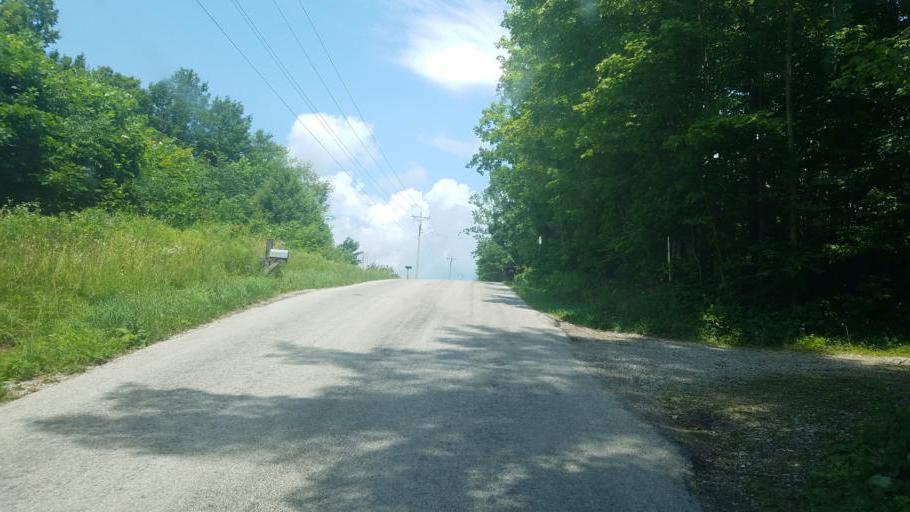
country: US
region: Ohio
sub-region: Richland County
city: Lexington
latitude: 40.5963
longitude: -82.6053
